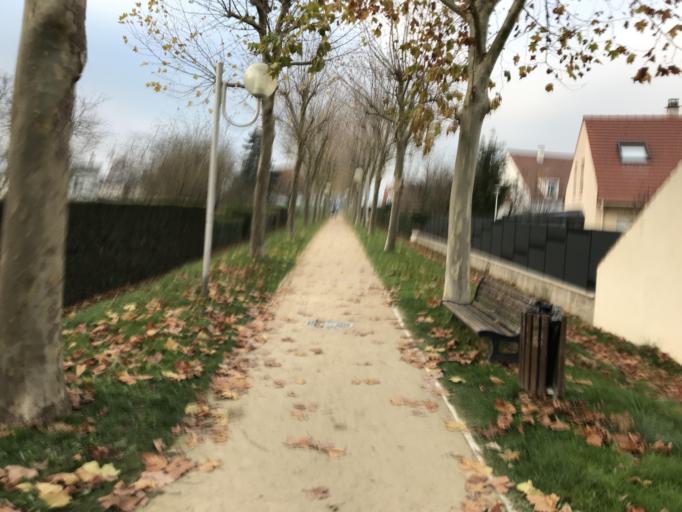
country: FR
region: Ile-de-France
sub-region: Departement de l'Essonne
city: Villiers-le-Bacle
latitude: 48.7283
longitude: 2.1220
